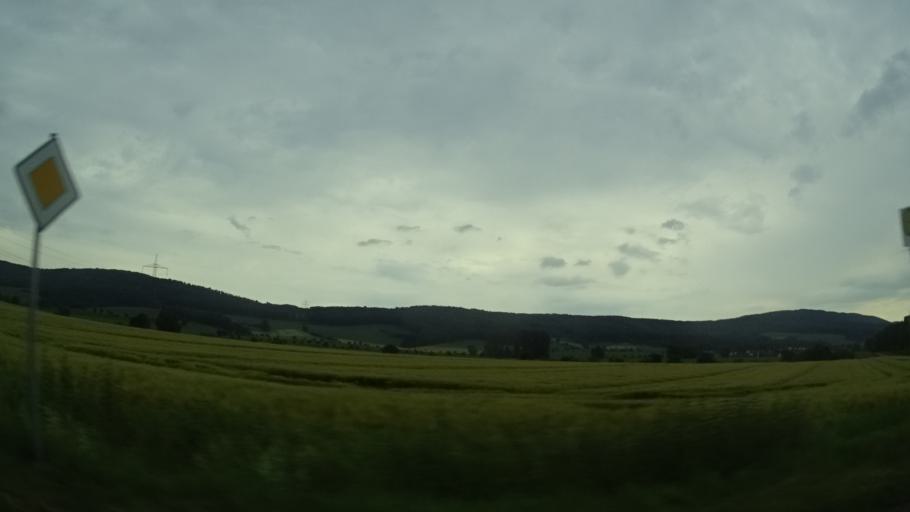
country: DE
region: Lower Saxony
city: Halle
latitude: 52.0130
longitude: 9.5577
